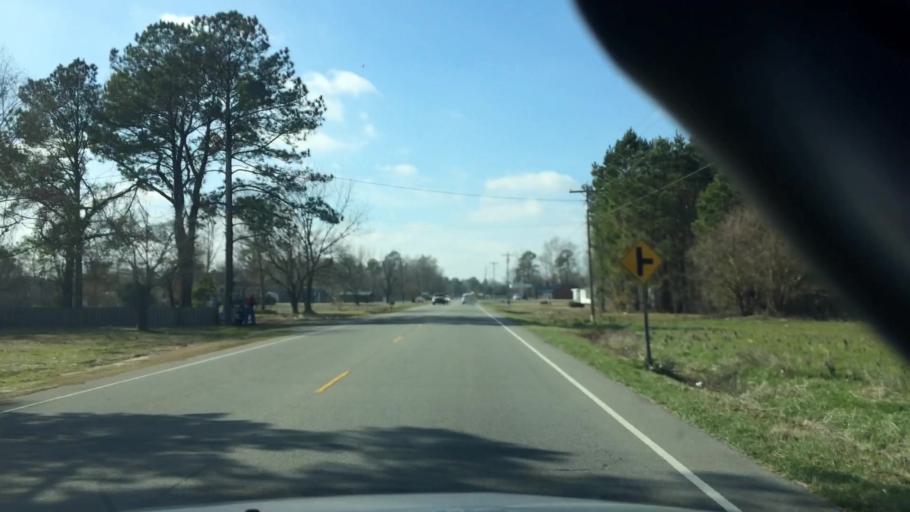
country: US
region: North Carolina
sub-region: Duplin County
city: Wallace
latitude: 34.7859
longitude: -77.9004
